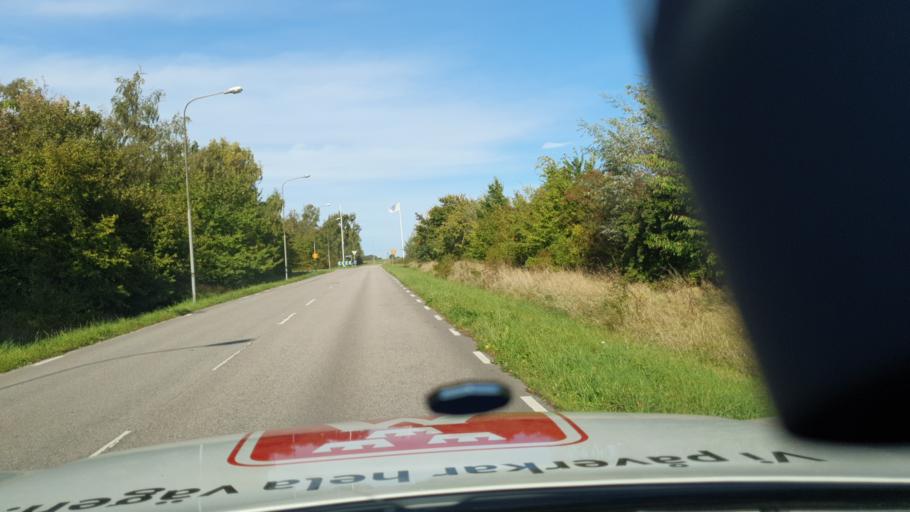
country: SE
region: Skane
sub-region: Vellinge Kommun
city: Vellinge
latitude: 55.4758
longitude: 13.0420
